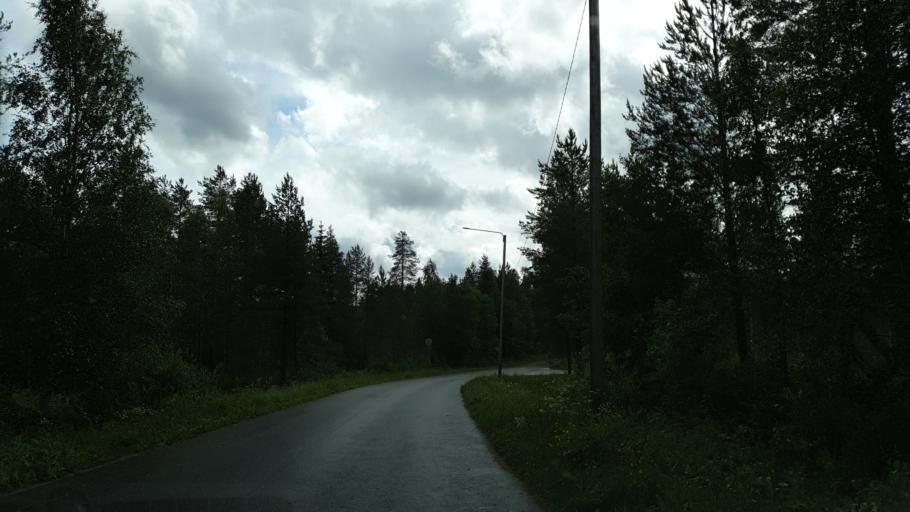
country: FI
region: Kainuu
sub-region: Kehys-Kainuu
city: Kuhmo
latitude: 64.1165
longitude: 29.5173
